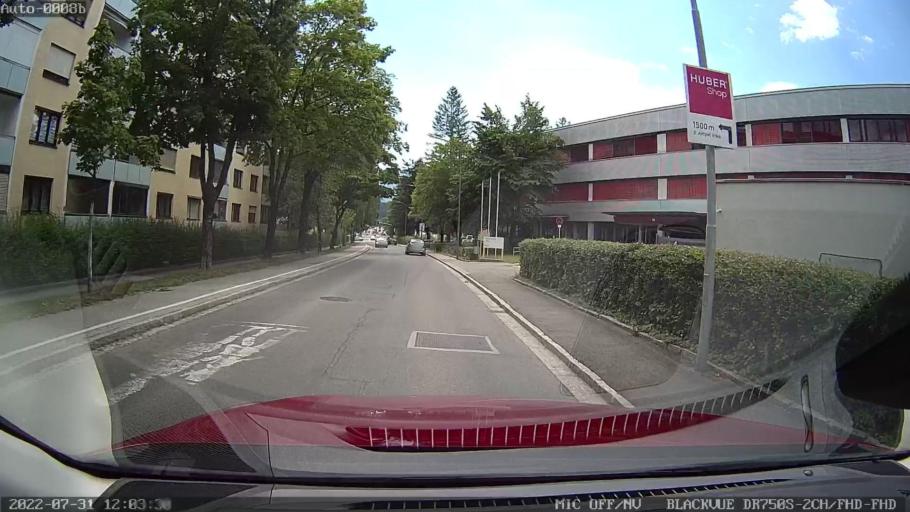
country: AT
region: Carinthia
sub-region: Villach Stadt
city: Villach
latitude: 46.6017
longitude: 13.8463
